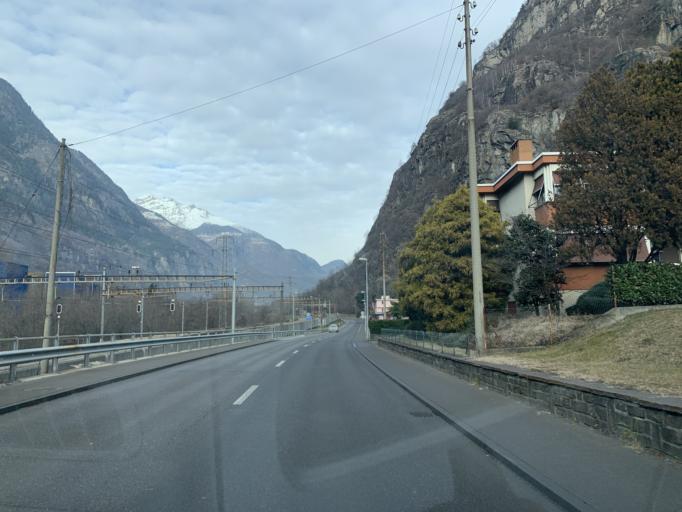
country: CH
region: Ticino
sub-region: Leventina District
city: Bodio
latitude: 46.3823
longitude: 8.9041
